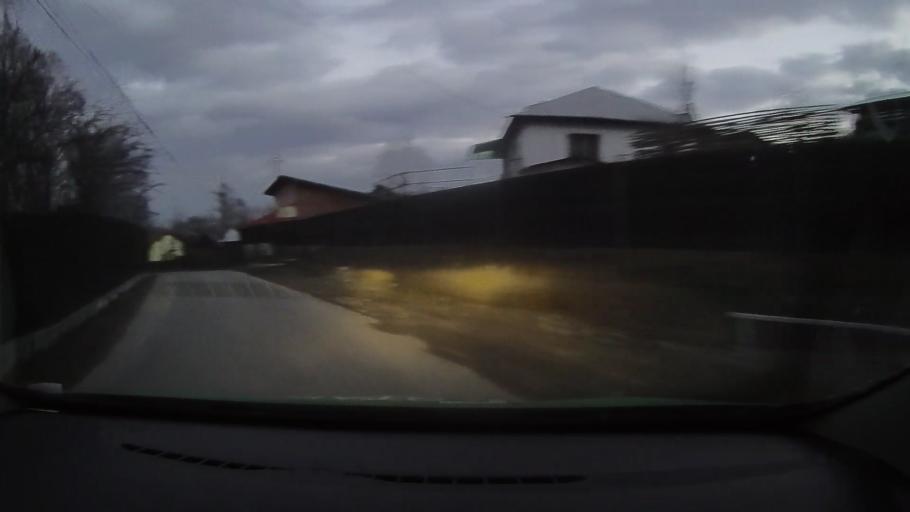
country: RO
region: Prahova
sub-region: Comuna Provita de Sus
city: Provita de Sus
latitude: 45.1386
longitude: 25.6311
